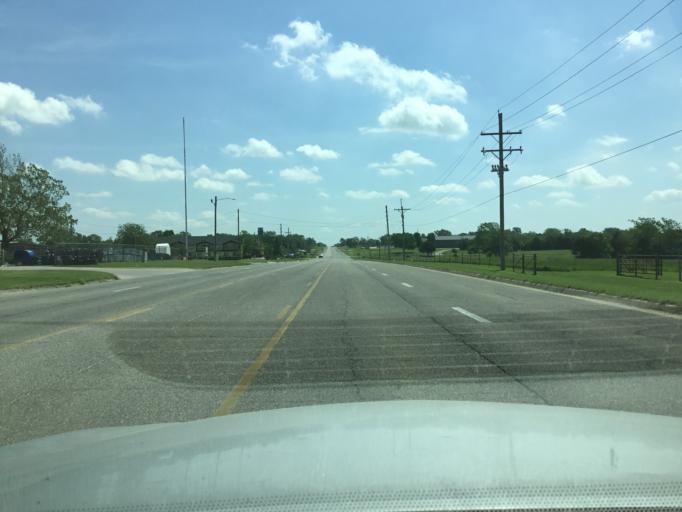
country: US
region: Kansas
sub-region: Labette County
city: Parsons
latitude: 37.3403
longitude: -95.2350
